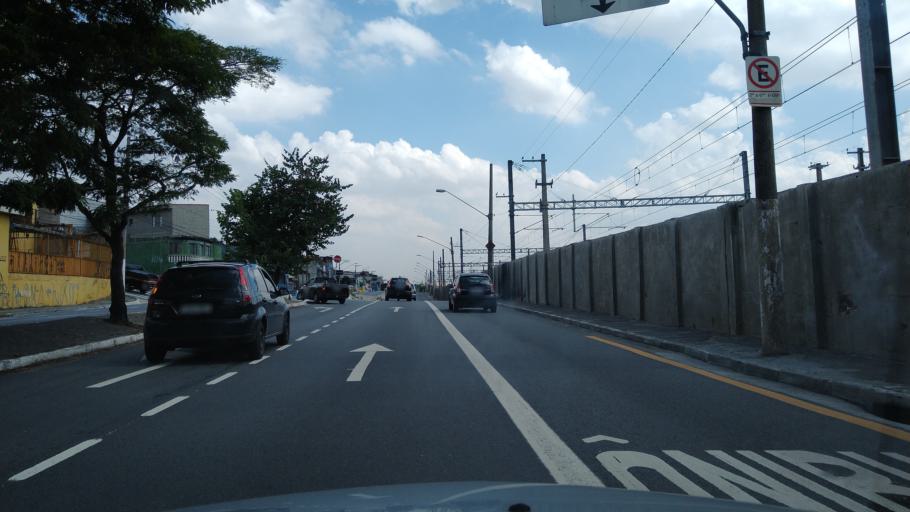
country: BR
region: Sao Paulo
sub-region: Guarulhos
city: Guarulhos
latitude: -23.5036
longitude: -46.5369
